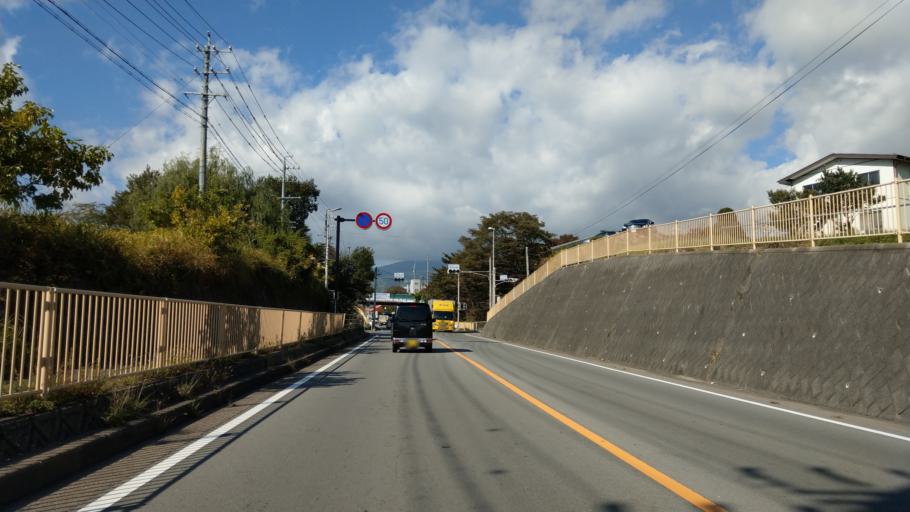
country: JP
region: Nagano
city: Komoro
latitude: 36.3229
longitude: 138.4364
